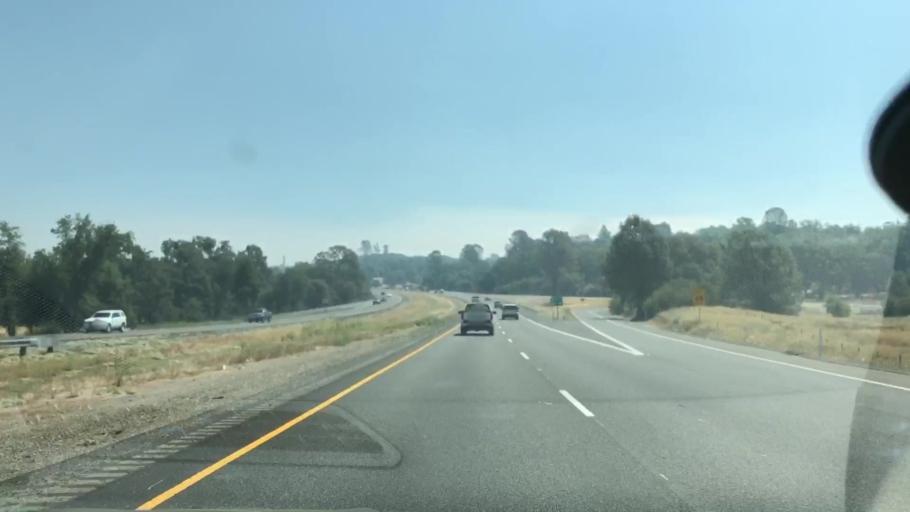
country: US
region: California
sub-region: El Dorado County
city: Shingle Springs
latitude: 38.6958
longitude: -120.8873
